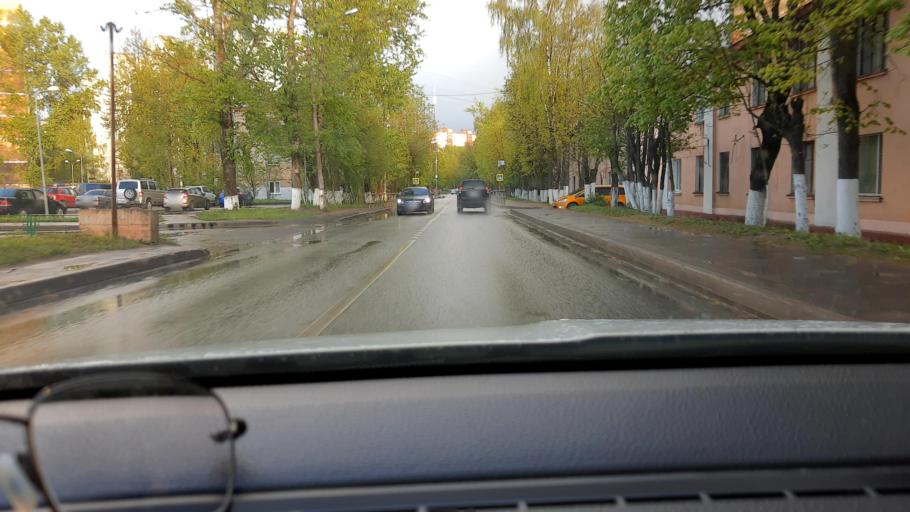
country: RU
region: Moskovskaya
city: Nakhabino
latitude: 55.8397
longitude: 37.1717
